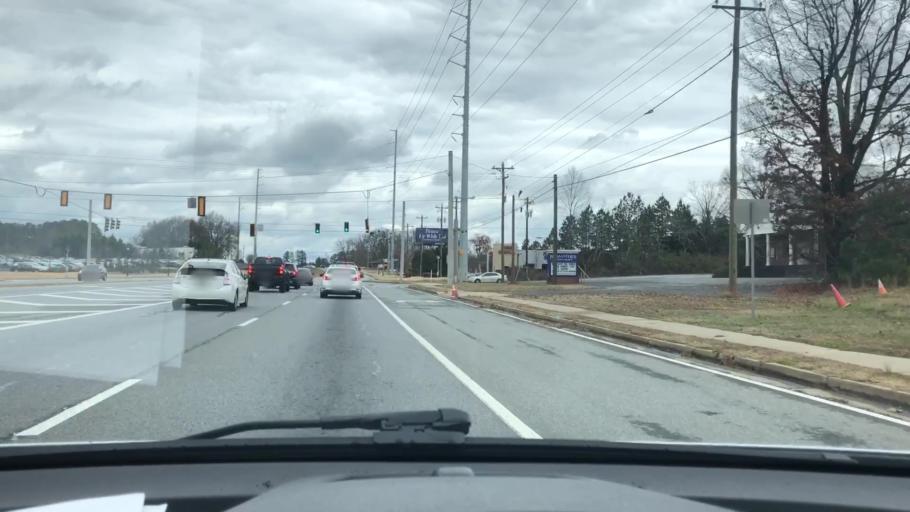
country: US
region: Georgia
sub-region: Forsyth County
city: Cumming
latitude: 34.1415
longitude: -84.1726
